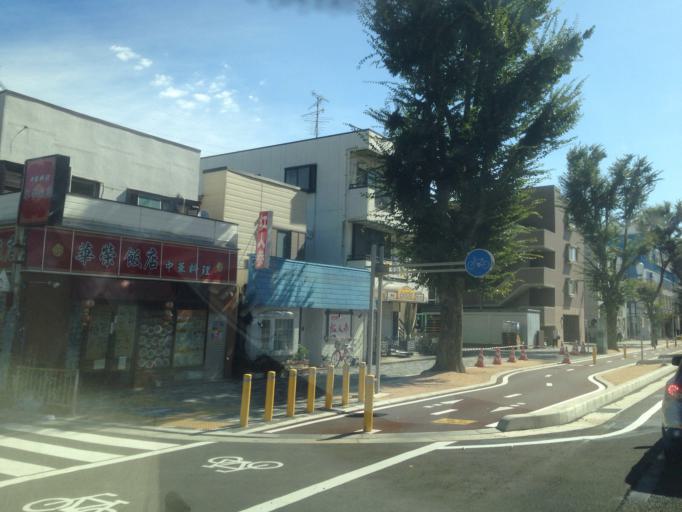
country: JP
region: Tokyo
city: Hachioji
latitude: 35.5774
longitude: 139.3647
